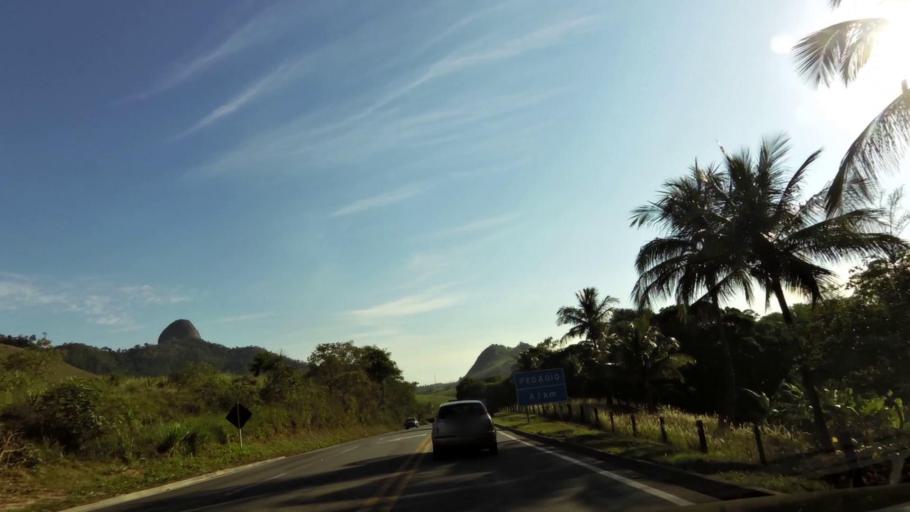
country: BR
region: Espirito Santo
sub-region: Guarapari
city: Guarapari
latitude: -20.5299
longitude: -40.4830
